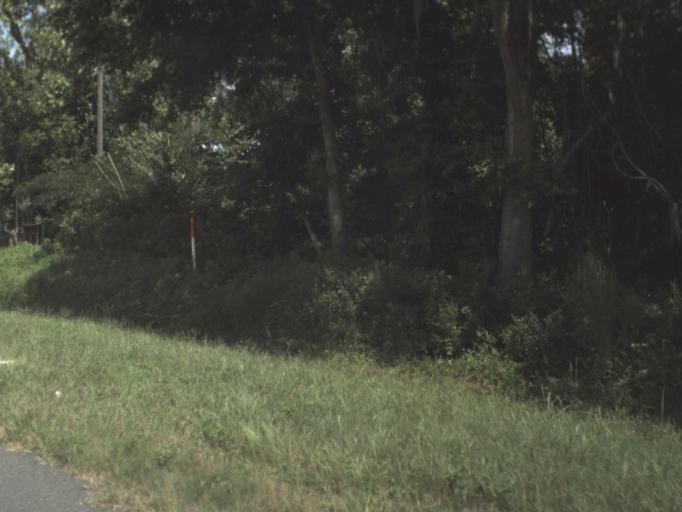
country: US
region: Florida
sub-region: Alachua County
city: Alachua
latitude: 29.8404
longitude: -82.3527
